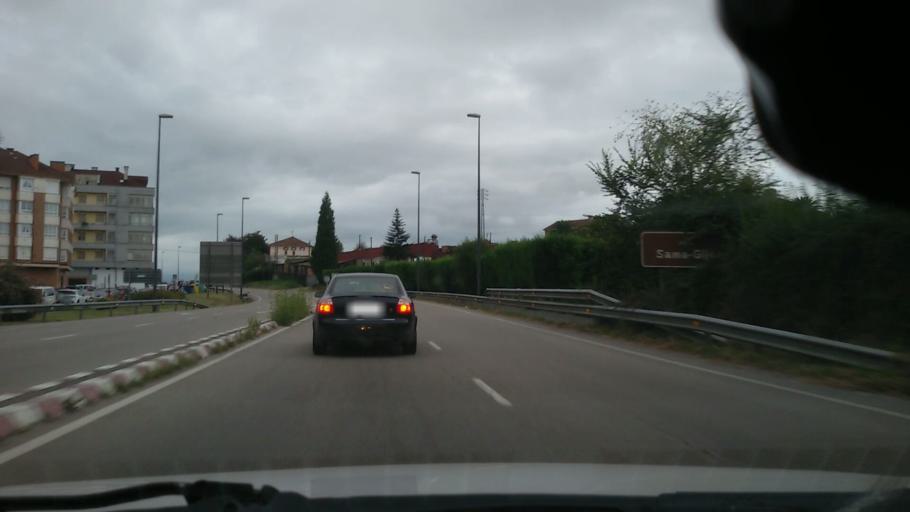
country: ES
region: Asturias
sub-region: Province of Asturias
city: Norena
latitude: 43.3859
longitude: -5.7025
